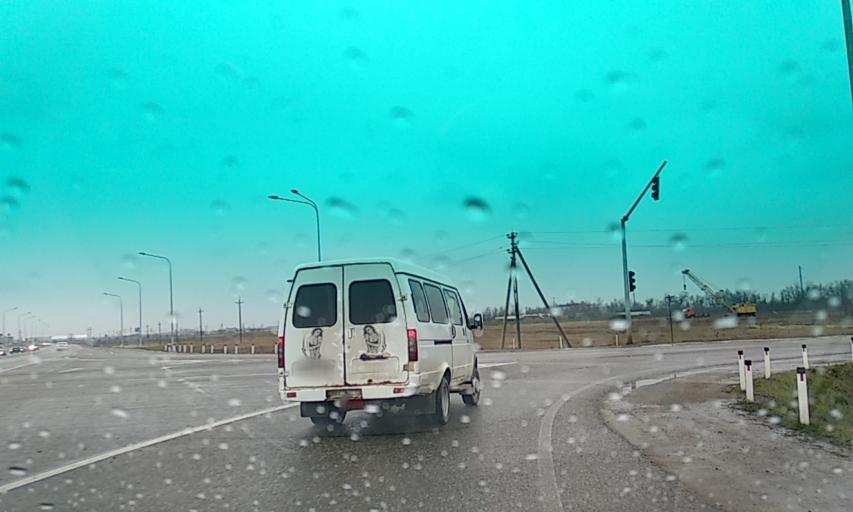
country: RU
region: Krasnodarskiy
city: Belorechensk
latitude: 44.8132
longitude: 39.8557
